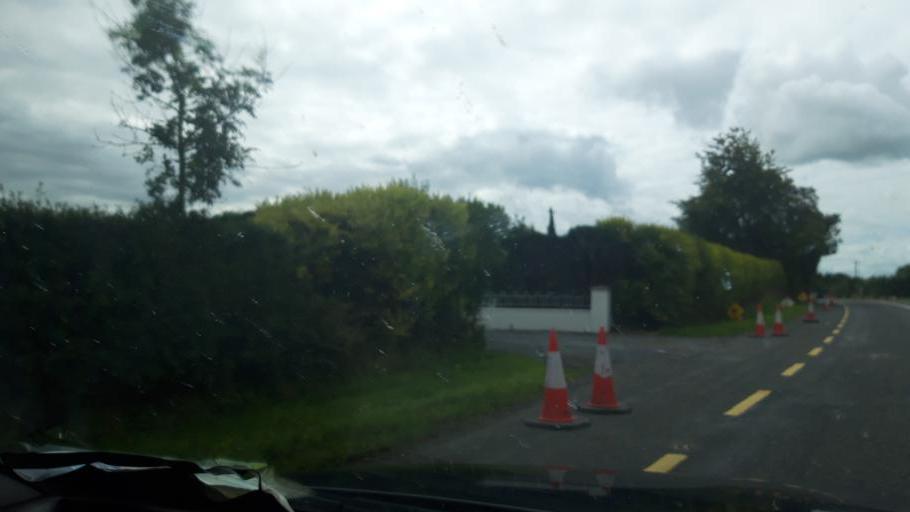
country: IE
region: Leinster
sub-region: Kilkenny
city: Kilkenny
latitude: 52.6034
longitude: -7.3021
